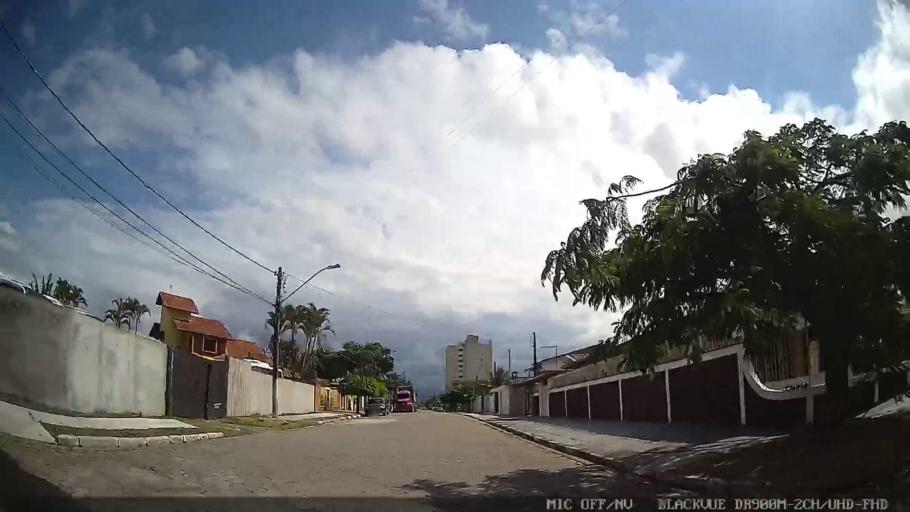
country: BR
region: Sao Paulo
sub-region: Caraguatatuba
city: Caraguatatuba
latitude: -23.6292
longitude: -45.4223
